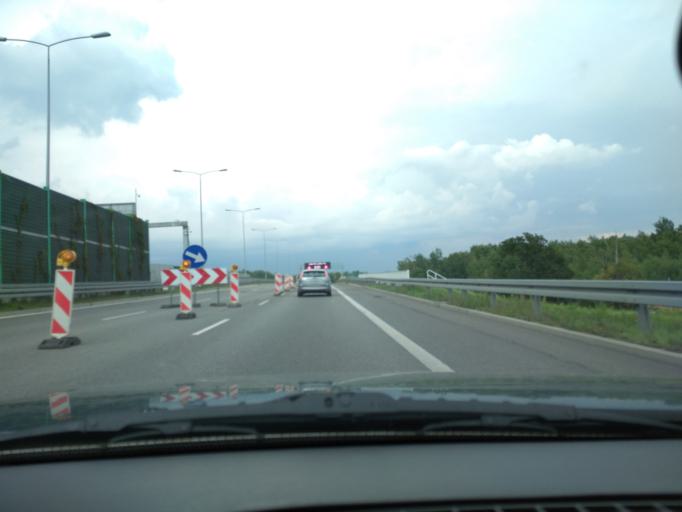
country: PL
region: Silesian Voivodeship
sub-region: Powiat gliwicki
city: Przyszowice
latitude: 50.2826
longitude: 18.7401
